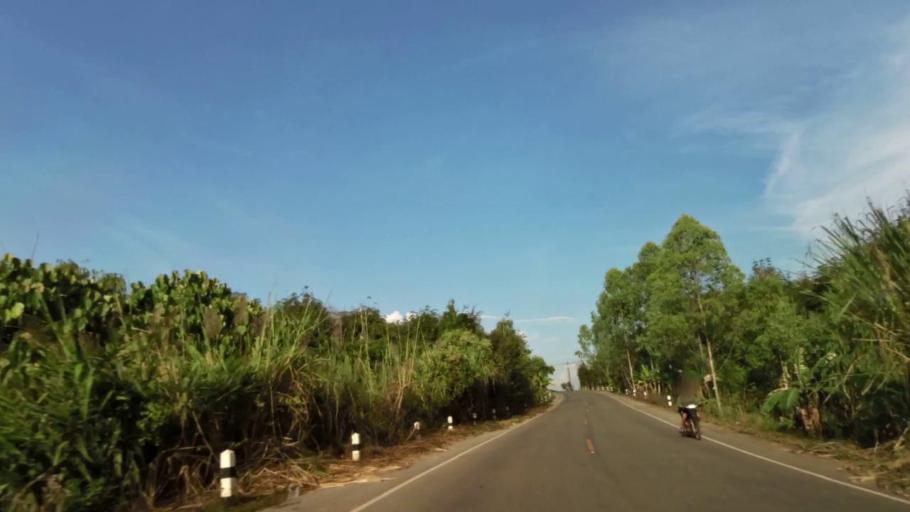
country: TH
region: Chiang Rai
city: Khun Tan
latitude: 19.8565
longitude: 100.3873
